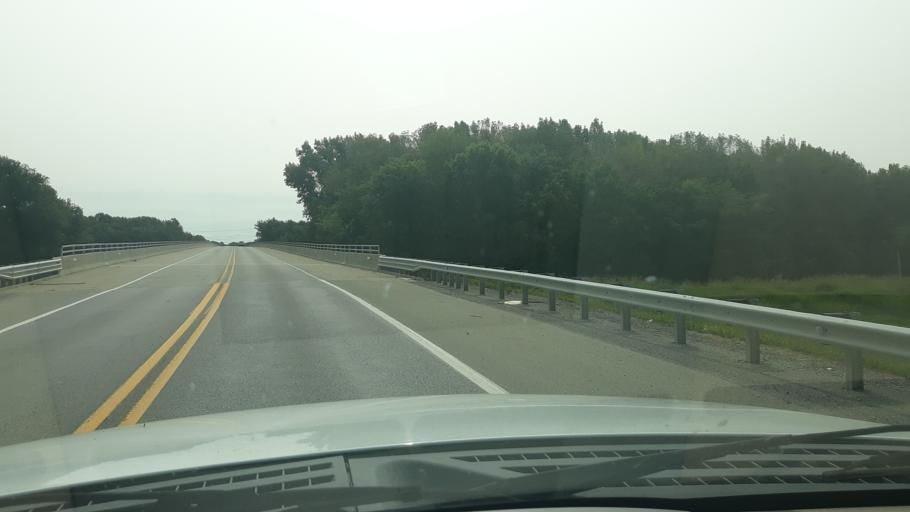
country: US
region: Illinois
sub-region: Wabash County
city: Mount Carmel
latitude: 38.4000
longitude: -87.7588
